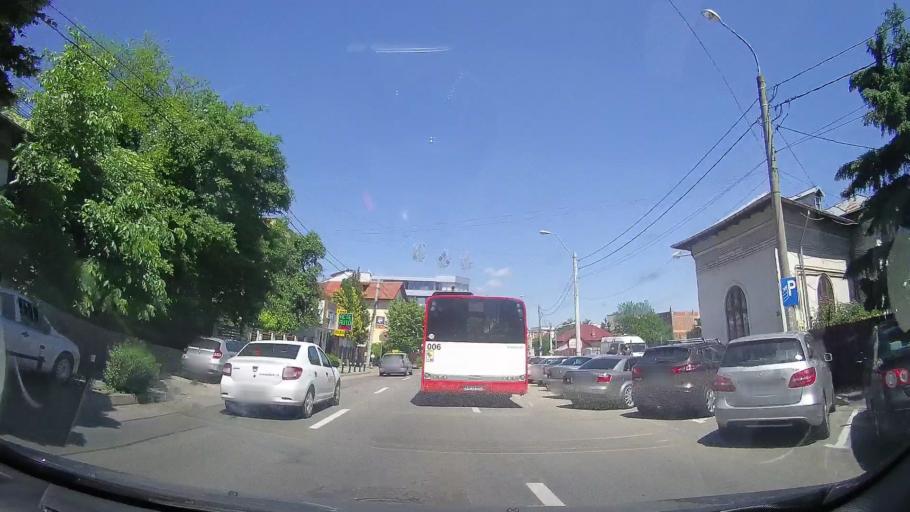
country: RO
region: Arges
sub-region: Comuna Albestii de Arges
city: Pitesti
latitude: 44.8619
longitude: 24.8654
